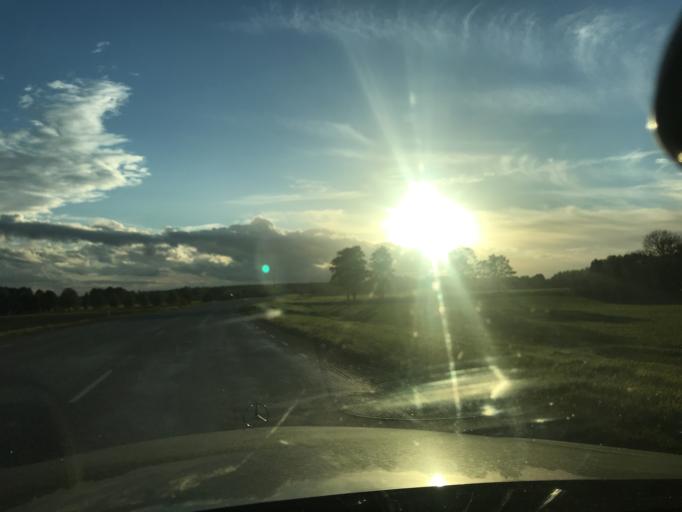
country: EE
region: Vorumaa
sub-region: Voru linn
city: Voru
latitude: 57.8659
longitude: 26.9229
